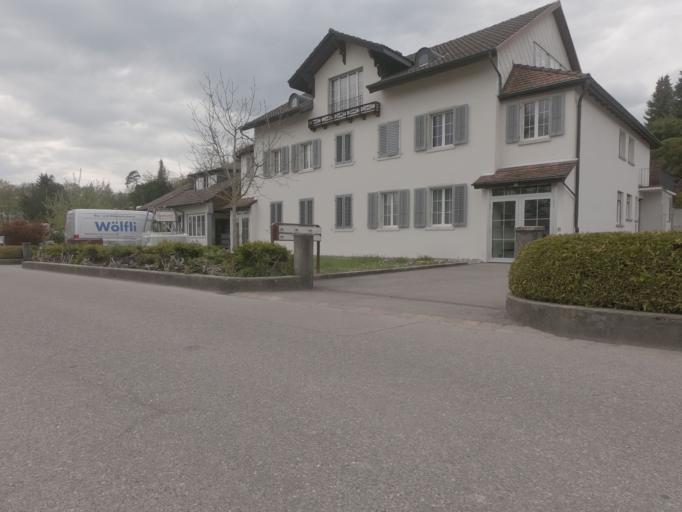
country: CH
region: Solothurn
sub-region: Bezirk Solothurn
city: Solothurn
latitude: 47.2229
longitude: 7.5458
